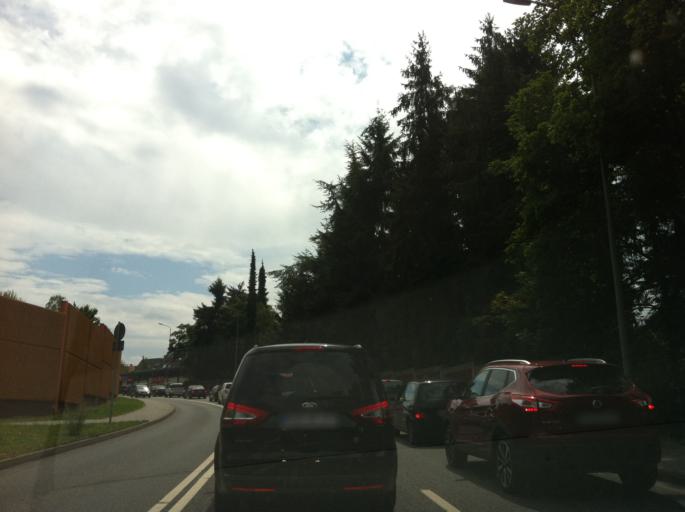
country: DE
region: Hesse
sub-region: Regierungsbezirk Darmstadt
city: Konigstein im Taunus
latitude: 50.1848
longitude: 8.4691
